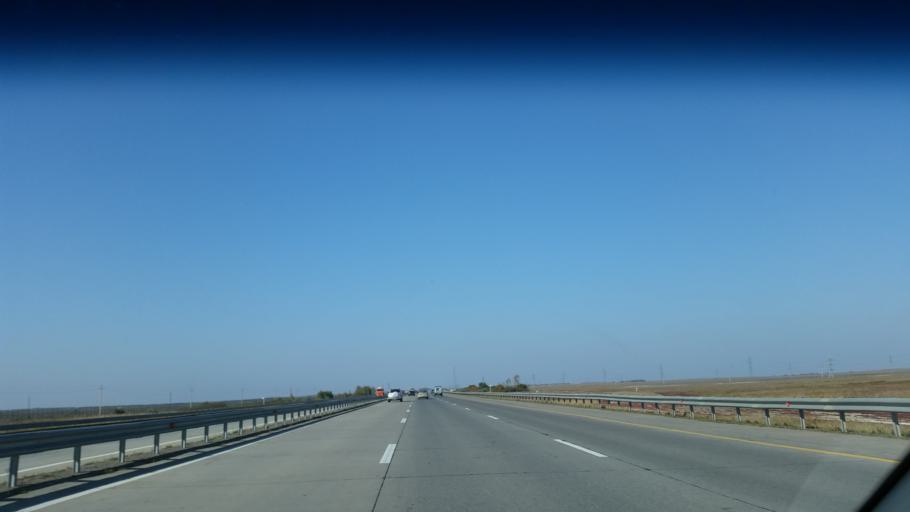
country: KZ
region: Astana Qalasy
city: Astana
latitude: 51.2756
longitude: 71.3655
